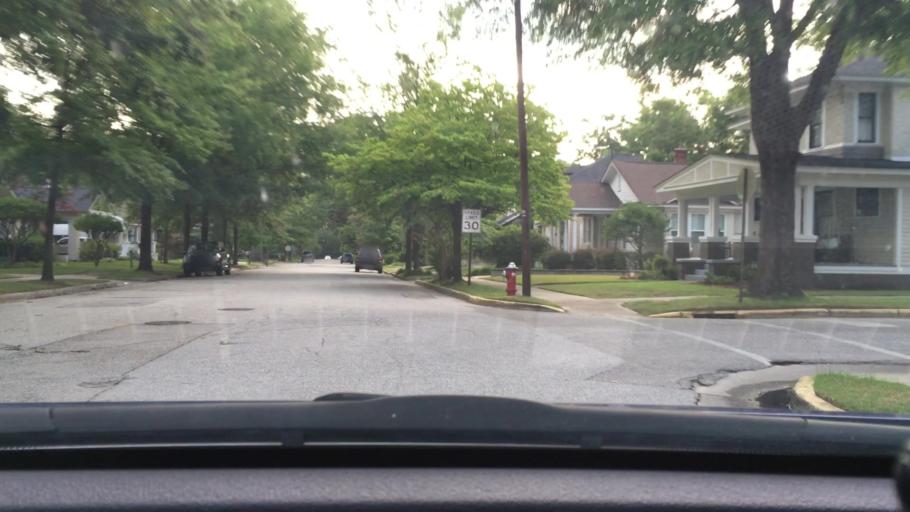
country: US
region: South Carolina
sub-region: Richland County
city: Columbia
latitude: 34.0212
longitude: -81.0416
